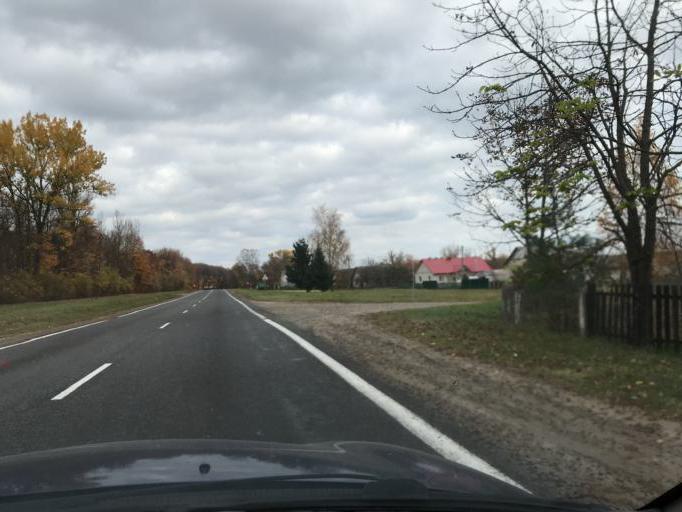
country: BY
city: Berezovka
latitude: 53.7447
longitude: 25.3768
